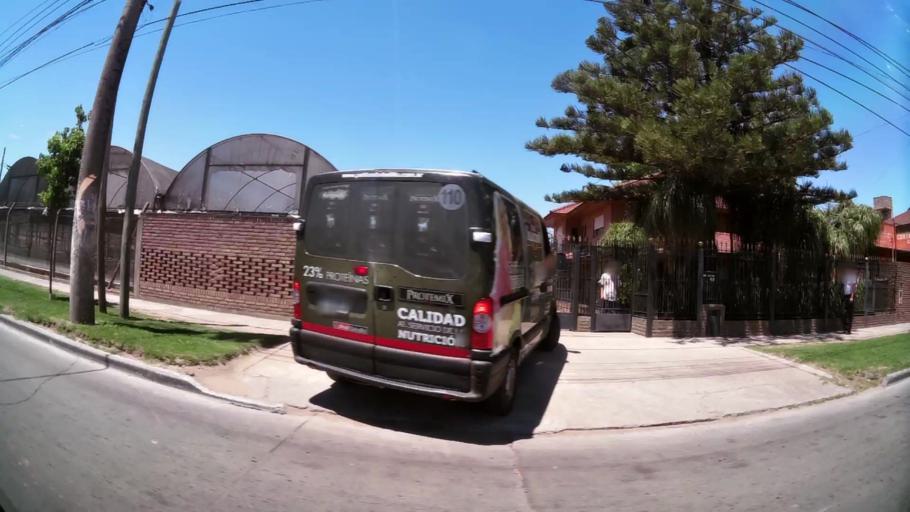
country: AR
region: Buenos Aires
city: Hurlingham
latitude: -34.5014
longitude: -58.7127
